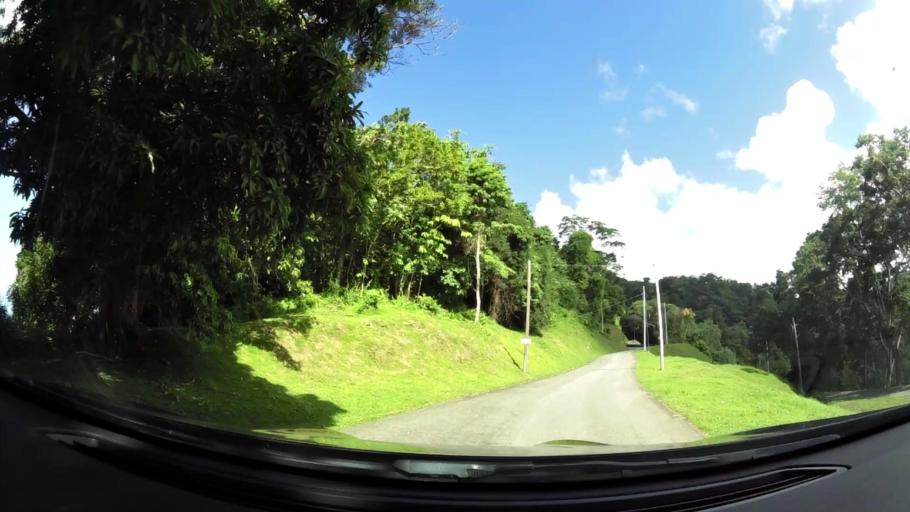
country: TT
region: Eastern Tobago
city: Roxborough
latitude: 11.3086
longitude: -60.6295
